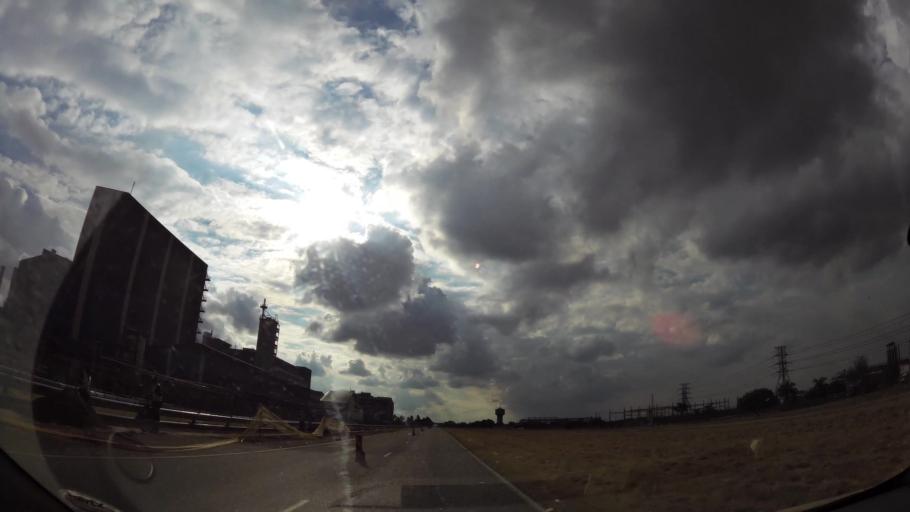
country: ZA
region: Orange Free State
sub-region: Fezile Dabi District Municipality
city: Sasolburg
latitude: -26.8223
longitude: 27.8457
